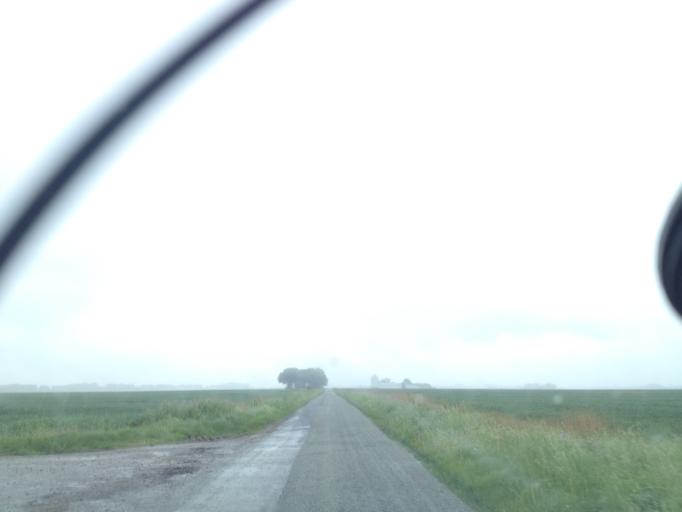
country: DE
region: Schleswig-Holstein
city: Klanxbull
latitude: 54.8796
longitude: 8.6915
